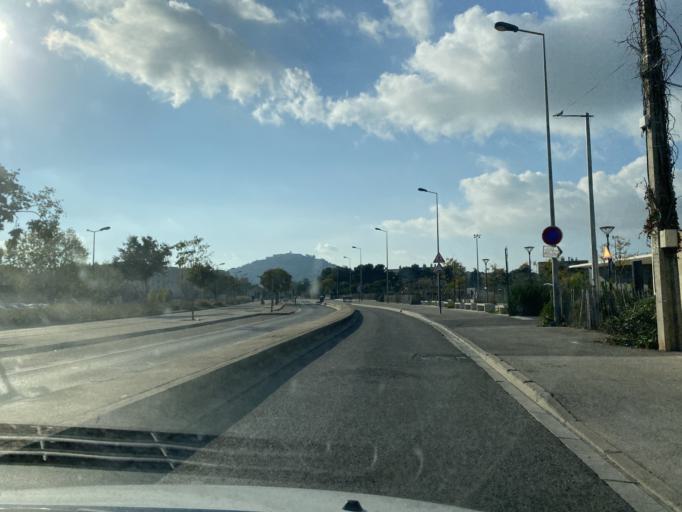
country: FR
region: Provence-Alpes-Cote d'Azur
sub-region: Departement du Var
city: Six-Fours-les-Plages
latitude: 43.1120
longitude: 5.8642
